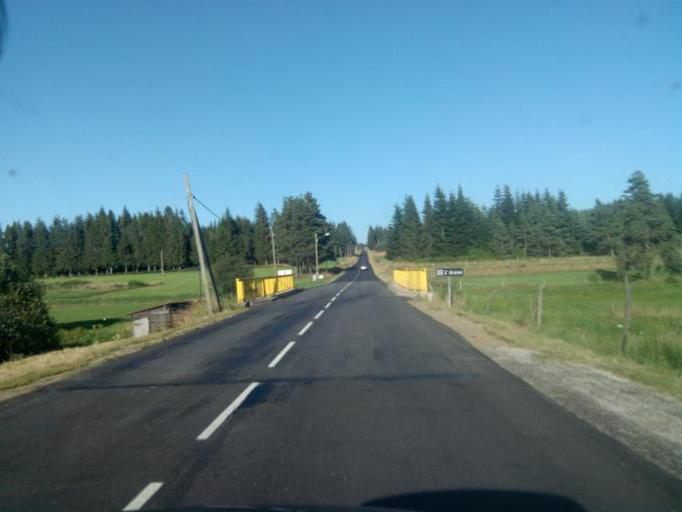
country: FR
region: Auvergne
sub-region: Departement de la Haute-Loire
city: Craponne-sur-Arzon
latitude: 45.3238
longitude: 3.8151
